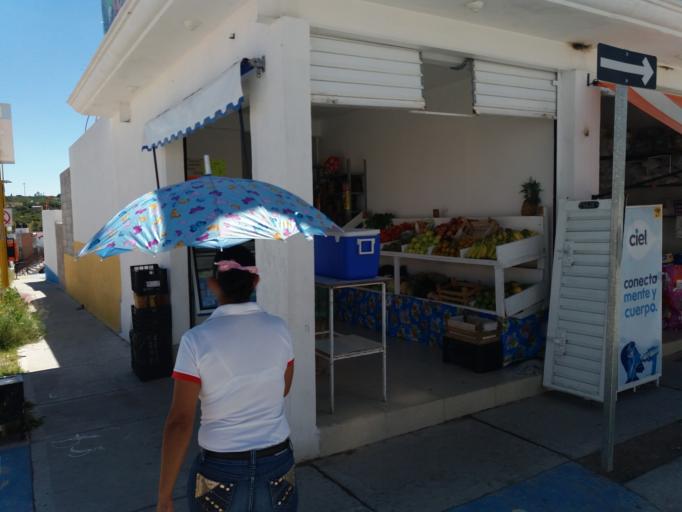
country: MX
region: Aguascalientes
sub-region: Aguascalientes
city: Cumbres III
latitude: 21.8724
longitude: -102.2291
